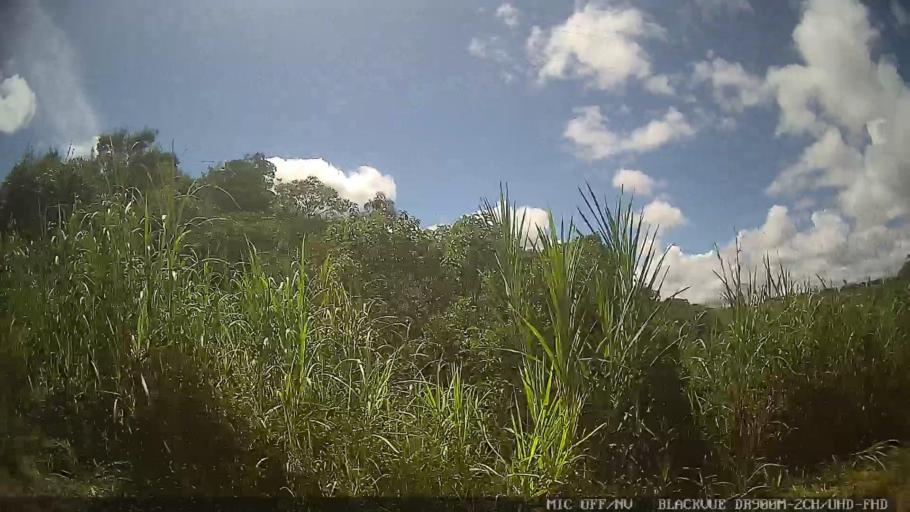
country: BR
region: Sao Paulo
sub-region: Amparo
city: Amparo
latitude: -22.8321
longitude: -46.7031
